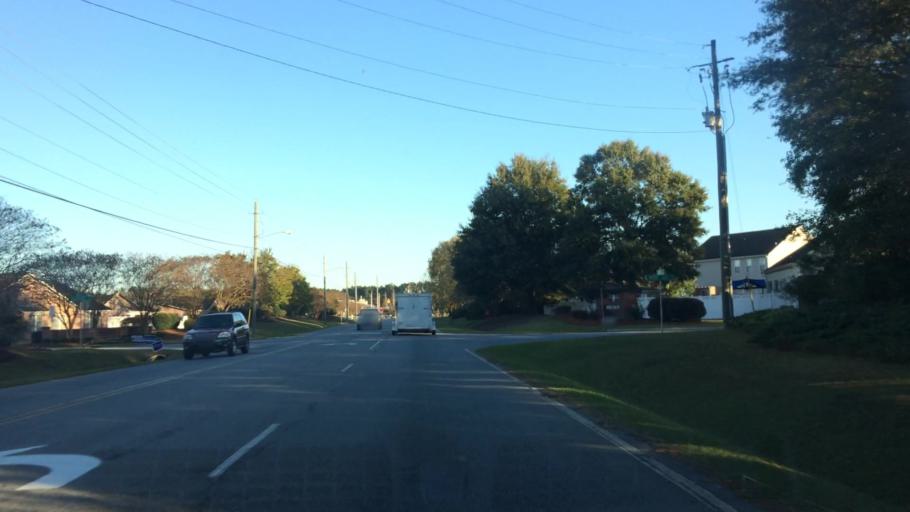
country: US
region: North Carolina
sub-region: Pitt County
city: Summerfield
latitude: 35.5571
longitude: -77.3858
